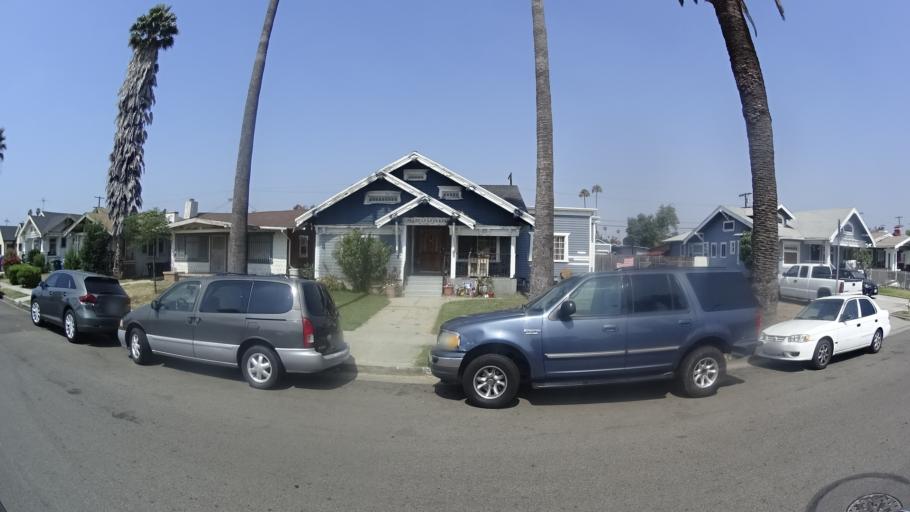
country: US
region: California
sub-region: Los Angeles County
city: View Park-Windsor Hills
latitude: 34.0213
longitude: -118.3213
